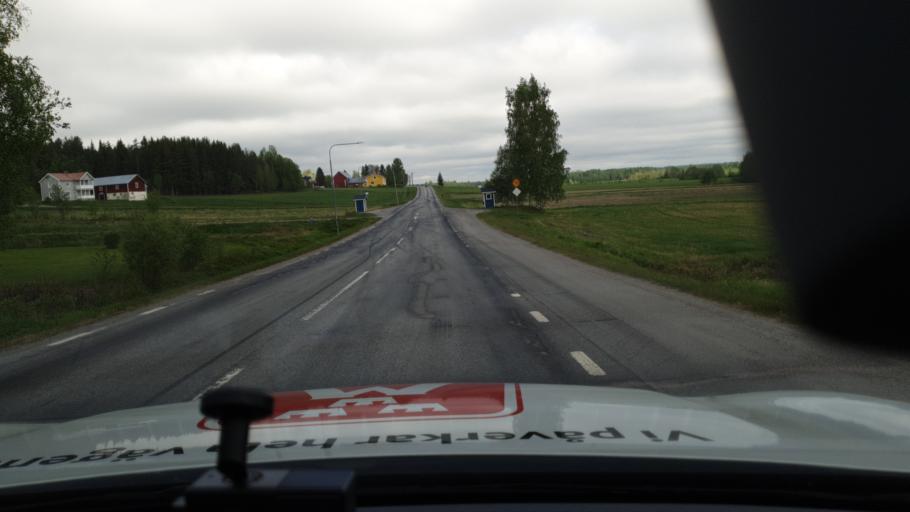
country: SE
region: Vaesterbotten
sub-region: Umea Kommun
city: Roback
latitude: 63.9143
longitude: 20.1971
